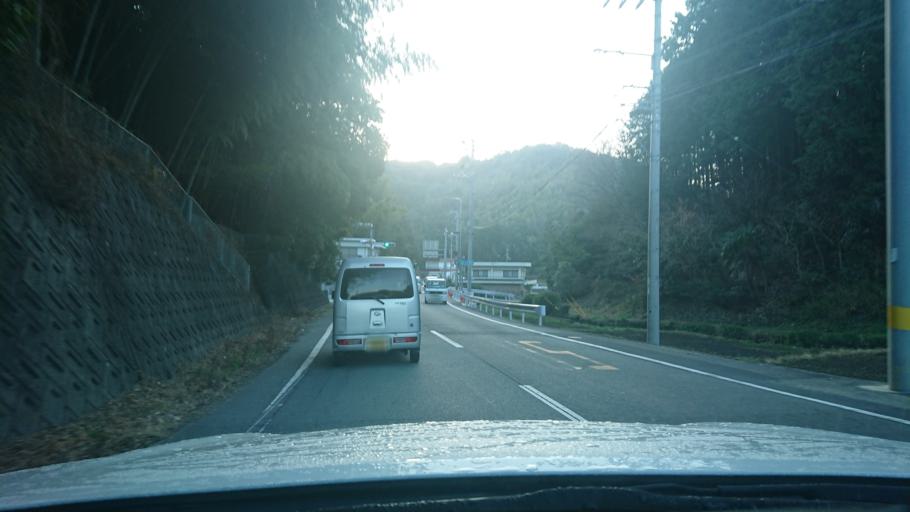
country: JP
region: Tokushima
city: Komatsushimacho
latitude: 33.9473
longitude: 134.5741
